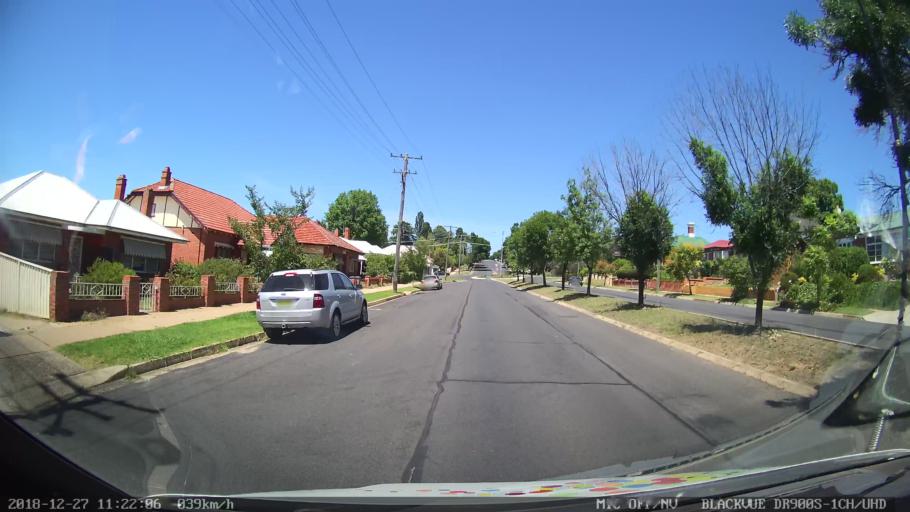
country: AU
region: New South Wales
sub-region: Bathurst Regional
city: Bathurst
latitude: -33.4234
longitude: 149.5730
